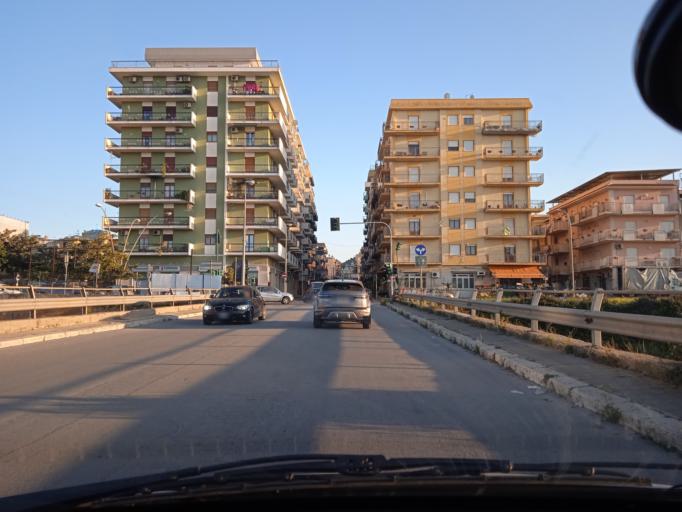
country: IT
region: Sicily
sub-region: Palermo
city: Bagheria
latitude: 38.0803
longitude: 13.5020
